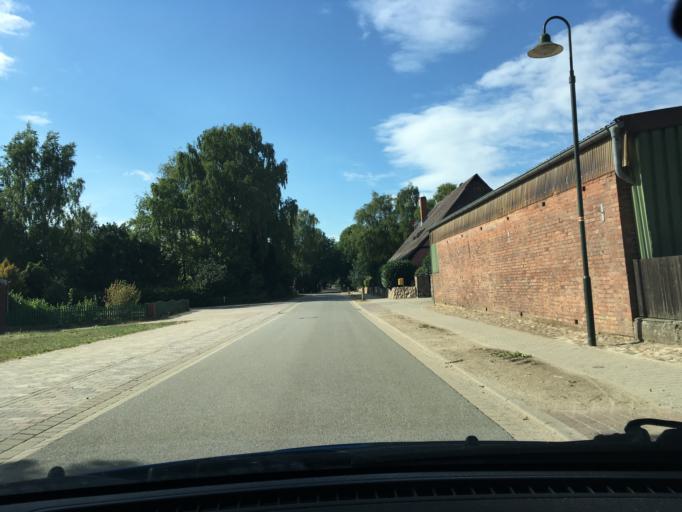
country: DE
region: Lower Saxony
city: Barum
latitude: 53.3589
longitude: 10.3955
